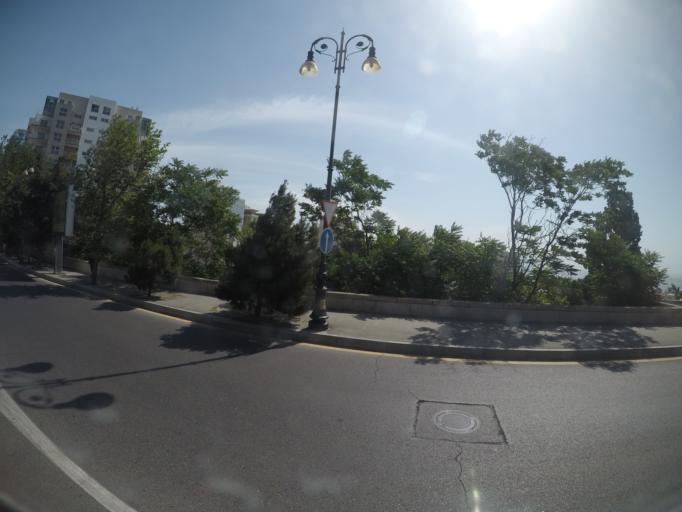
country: AZ
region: Baki
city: Badamdar
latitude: 40.3678
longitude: 49.8248
